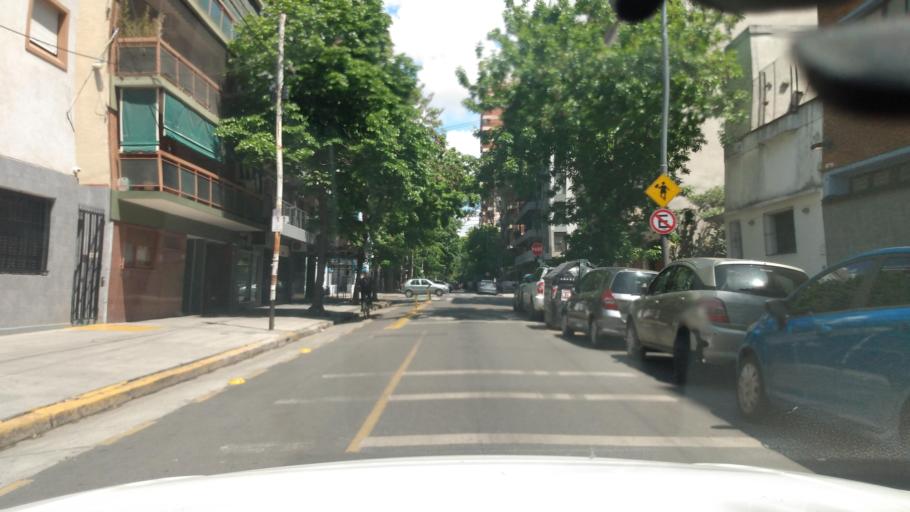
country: AR
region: Buenos Aires F.D.
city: Villa Santa Rita
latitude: -34.5759
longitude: -58.4871
